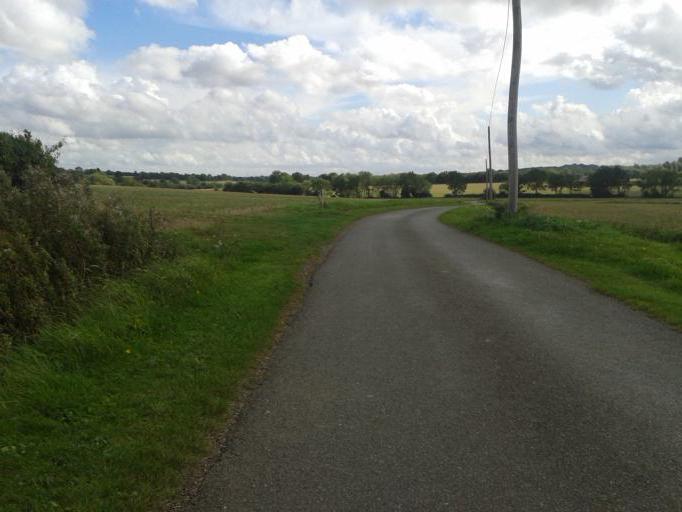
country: GB
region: England
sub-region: Hertfordshire
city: Reed
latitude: 51.9857
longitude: 0.0892
